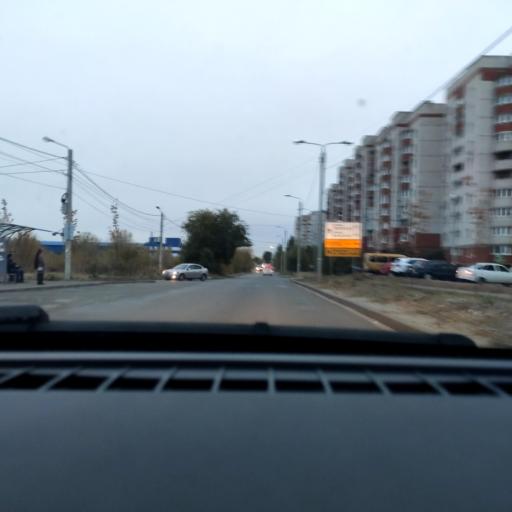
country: RU
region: Voronezj
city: Somovo
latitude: 51.6733
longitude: 39.2910
